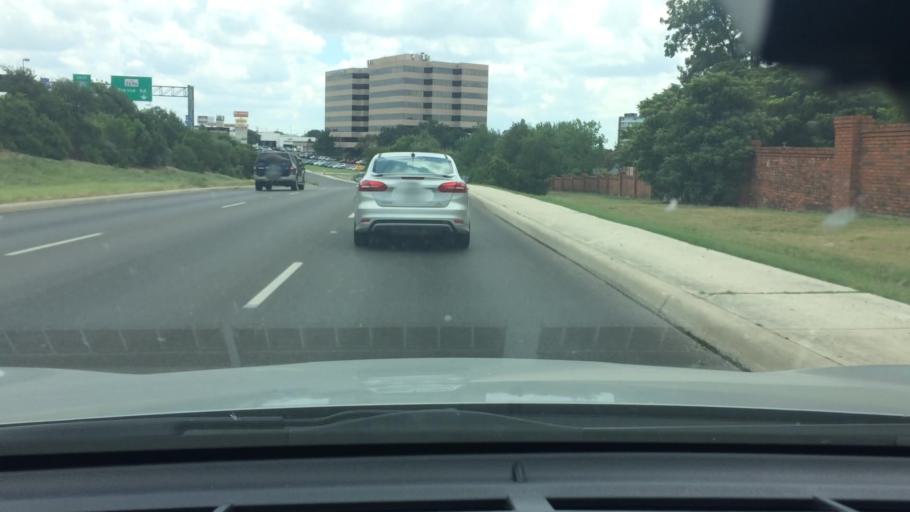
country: US
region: Texas
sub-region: Bexar County
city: Castle Hills
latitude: 29.5199
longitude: -98.5124
